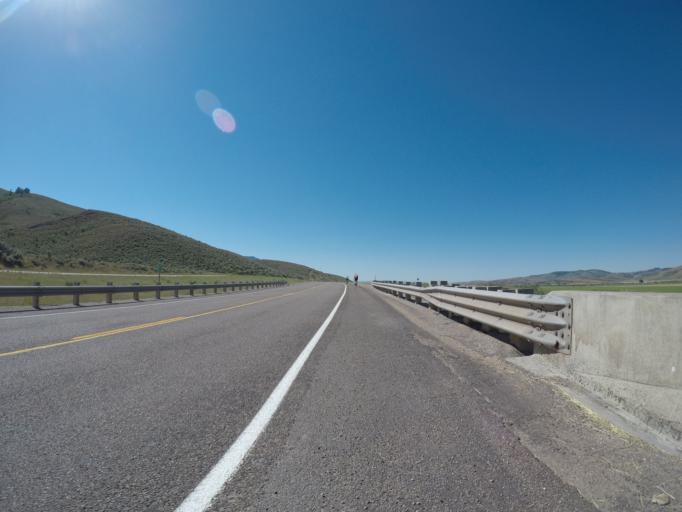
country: US
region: Idaho
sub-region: Bear Lake County
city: Montpelier
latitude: 42.3867
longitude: -111.0533
